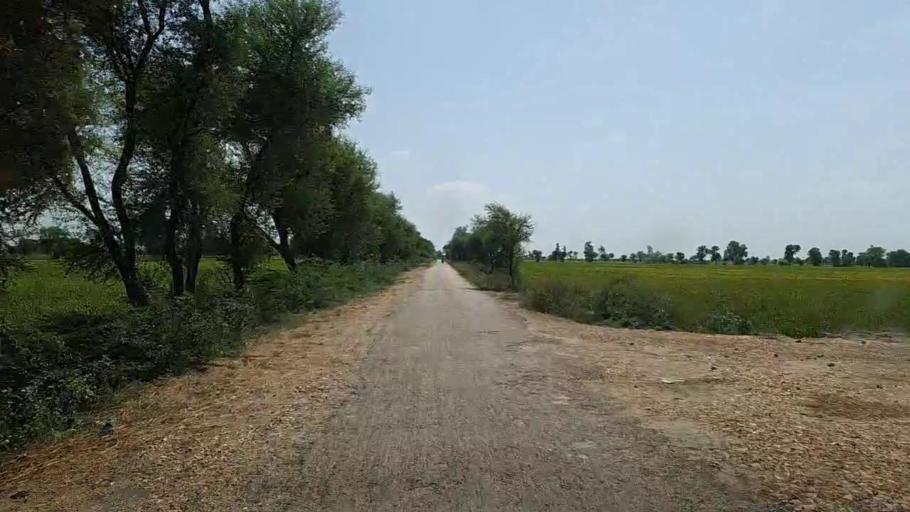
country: PK
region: Sindh
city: Kario
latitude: 24.6490
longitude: 68.5641
